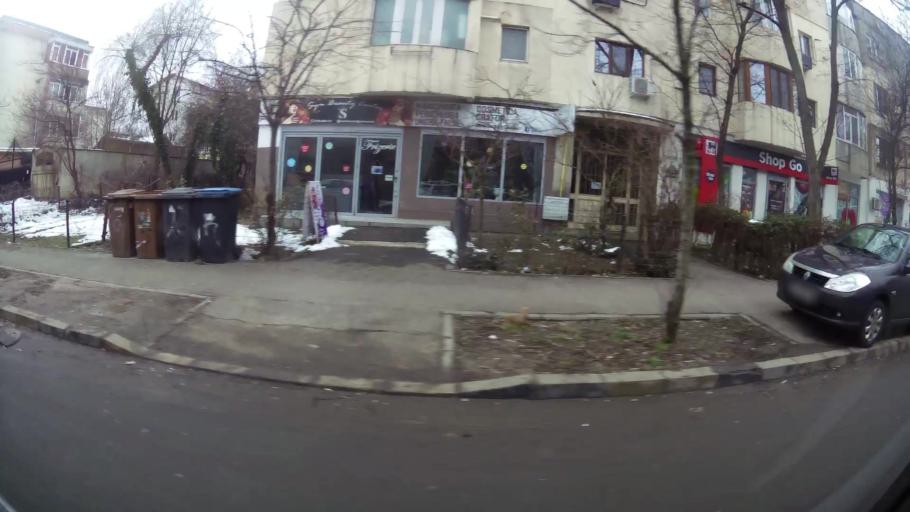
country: RO
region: Ilfov
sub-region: Comuna Chiajna
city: Rosu
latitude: 44.4396
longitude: 26.0053
